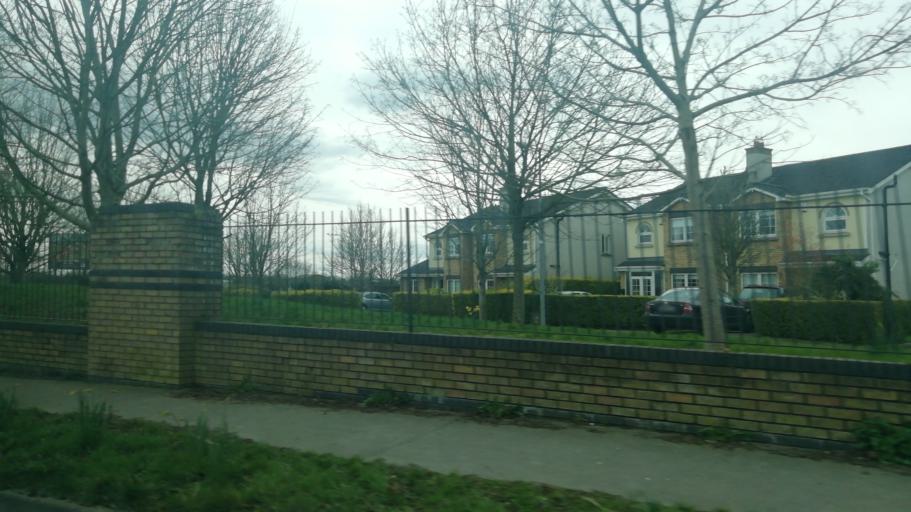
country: IE
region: Leinster
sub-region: Kildare
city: Clane
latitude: 53.2947
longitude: -6.6935
